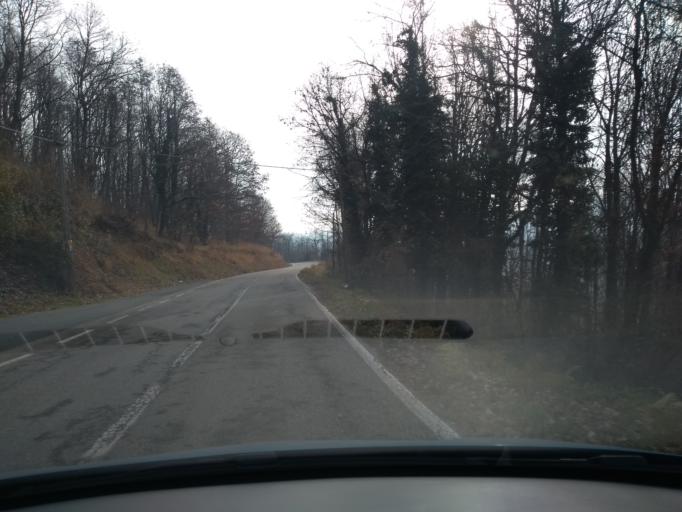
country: IT
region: Piedmont
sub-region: Provincia di Torino
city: Balangero
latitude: 45.2795
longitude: 7.5048
